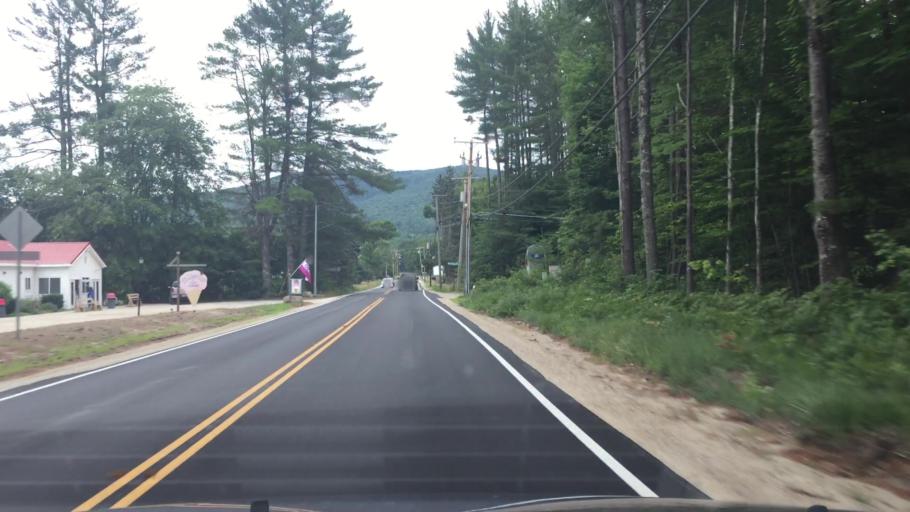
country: US
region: New Hampshire
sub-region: Carroll County
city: Freedom
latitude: 43.8012
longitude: -71.0587
